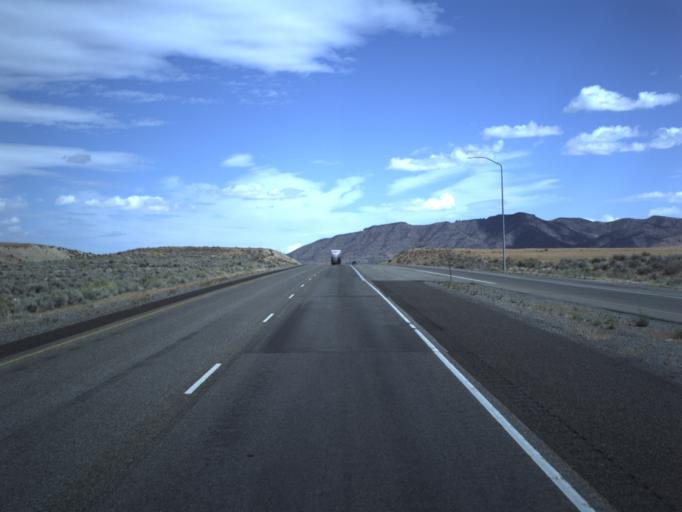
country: US
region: Utah
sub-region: Tooele County
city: Grantsville
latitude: 40.7587
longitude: -113.0146
